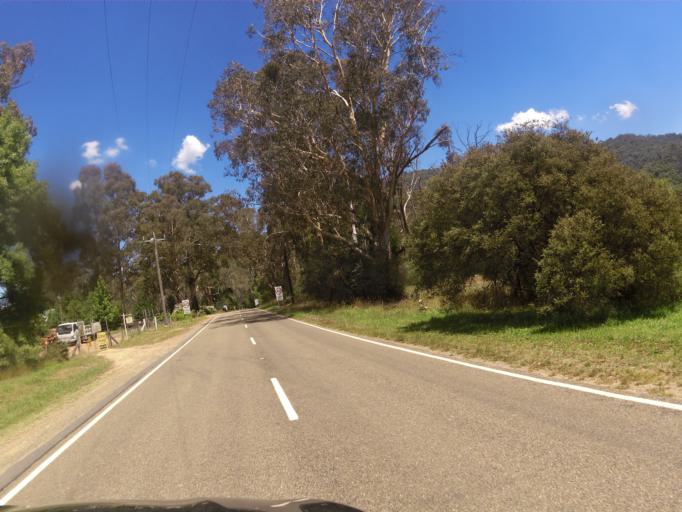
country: AU
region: Victoria
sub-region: Alpine
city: Mount Beauty
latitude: -36.7392
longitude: 147.0151
